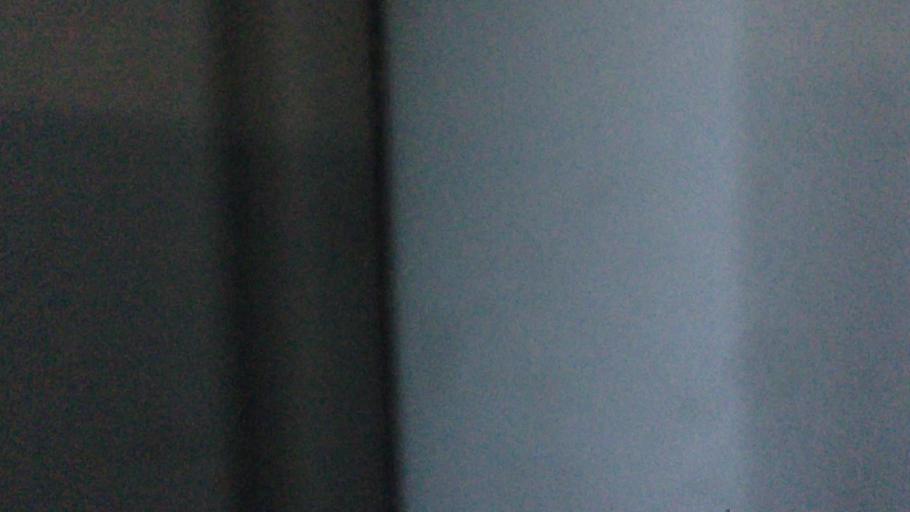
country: US
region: New York
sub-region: Dutchess County
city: Rhinebeck
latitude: 41.9536
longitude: -73.9184
